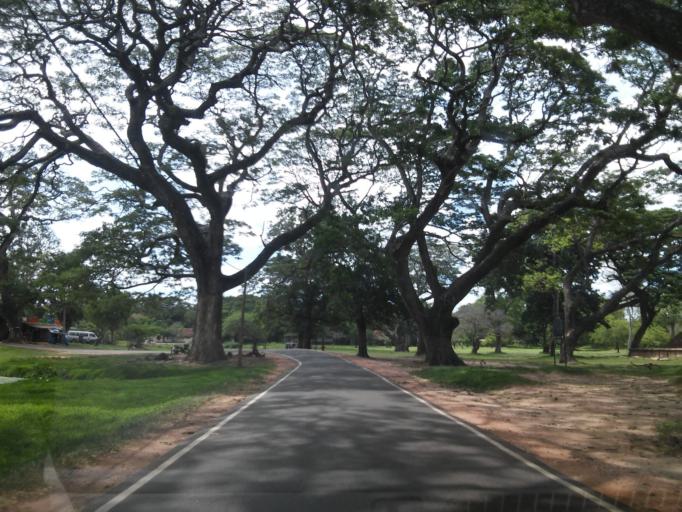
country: LK
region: North Central
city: Anuradhapura
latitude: 8.3506
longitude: 80.3992
